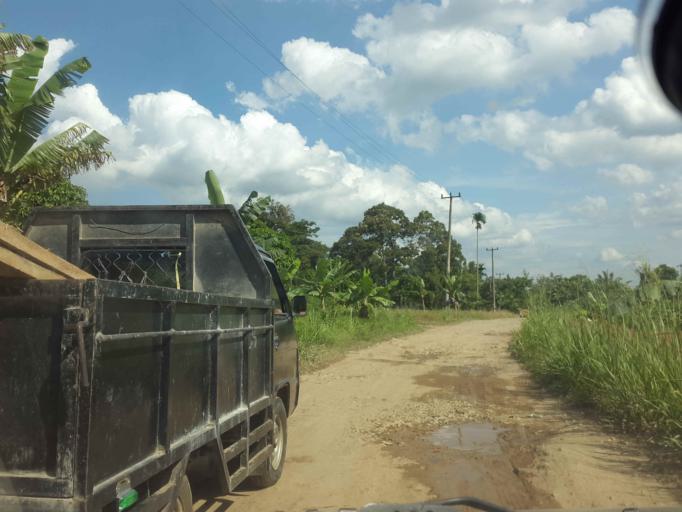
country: ID
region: Lampung
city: Panjang
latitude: -5.4163
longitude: 105.3478
